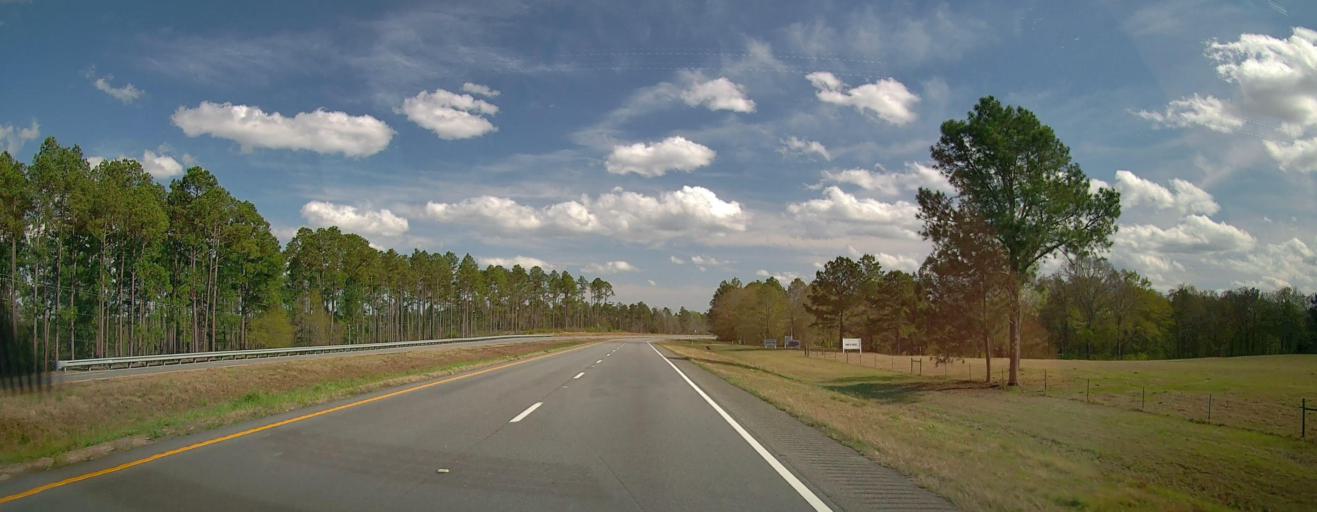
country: US
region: Georgia
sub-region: Baldwin County
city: Hardwick
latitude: 32.9977
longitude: -83.2156
